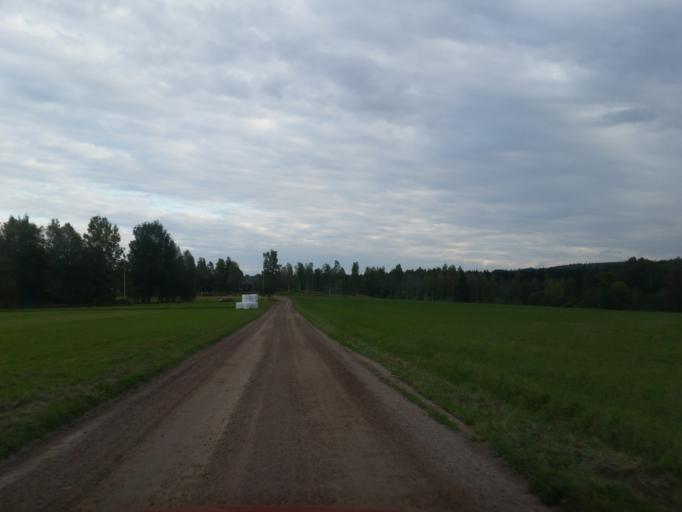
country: SE
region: Dalarna
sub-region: Leksand Municipality
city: Smedby
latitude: 60.6783
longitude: 15.1383
